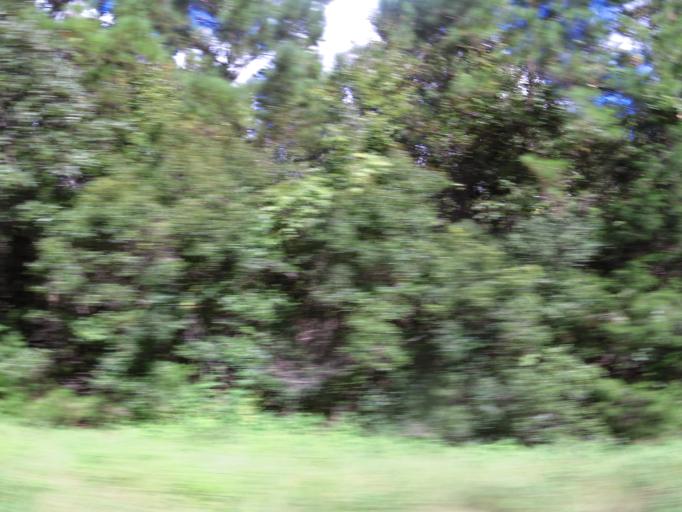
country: US
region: Georgia
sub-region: Camden County
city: Kingsland
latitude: 30.7564
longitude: -81.6874
